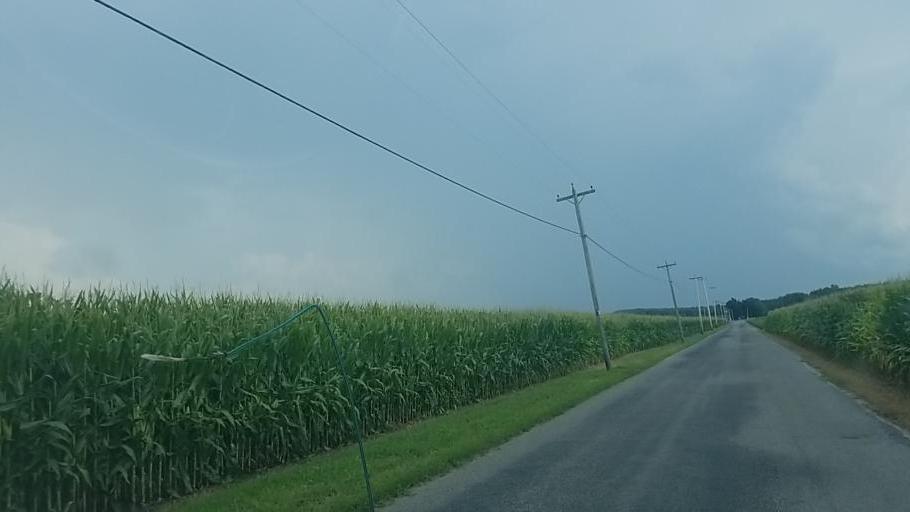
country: US
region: Ohio
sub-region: Medina County
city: Lodi
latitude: 41.0063
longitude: -82.0188
